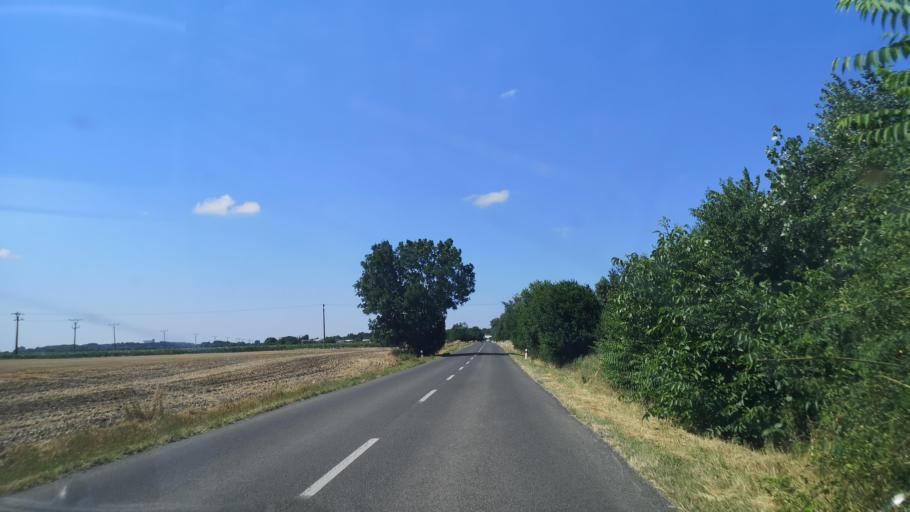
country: SK
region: Trnavsky
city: Dunajska Streda
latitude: 48.0645
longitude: 17.4767
